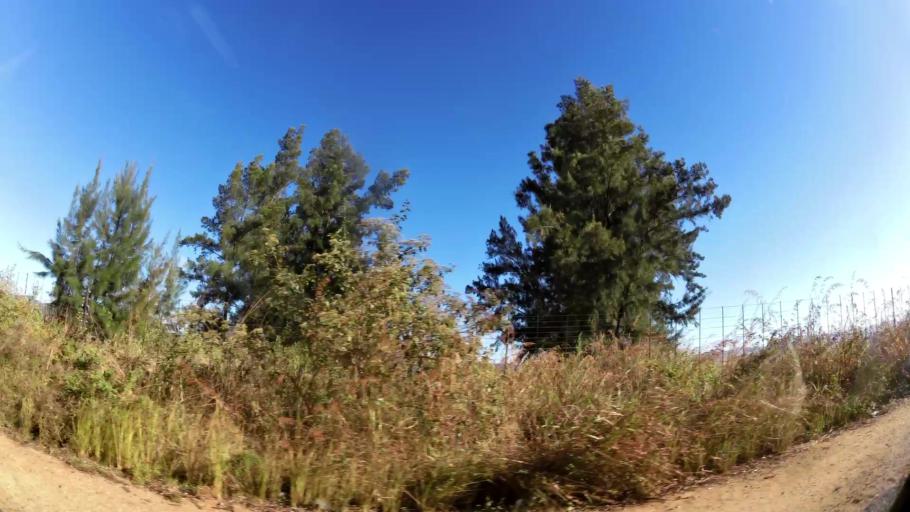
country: ZA
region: Limpopo
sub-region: Mopani District Municipality
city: Tzaneen
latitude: -23.8400
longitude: 30.1304
